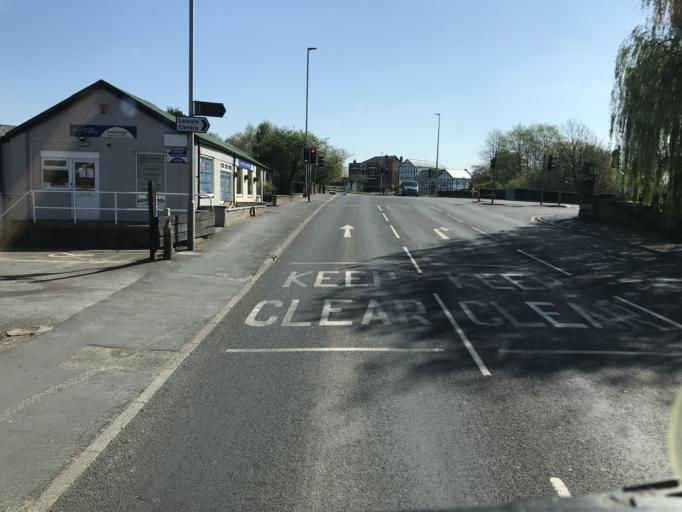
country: GB
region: England
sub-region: Cheshire East
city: Middlewich
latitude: 53.1930
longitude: -2.4446
